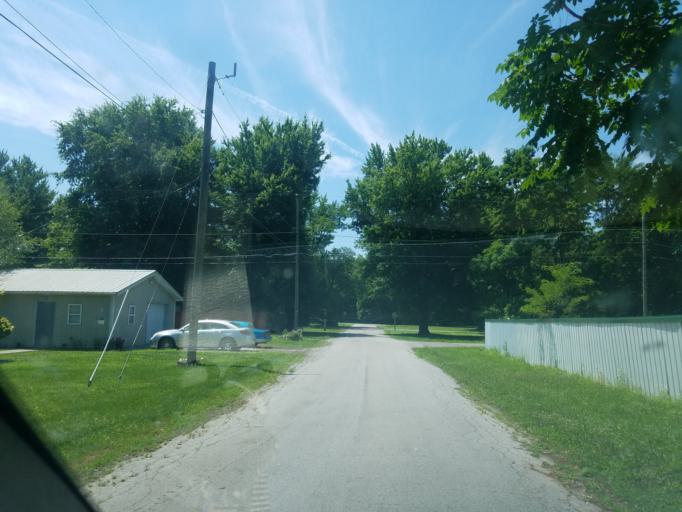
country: US
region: Ohio
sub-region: Hardin County
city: Kenton
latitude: 40.6426
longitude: -83.6198
